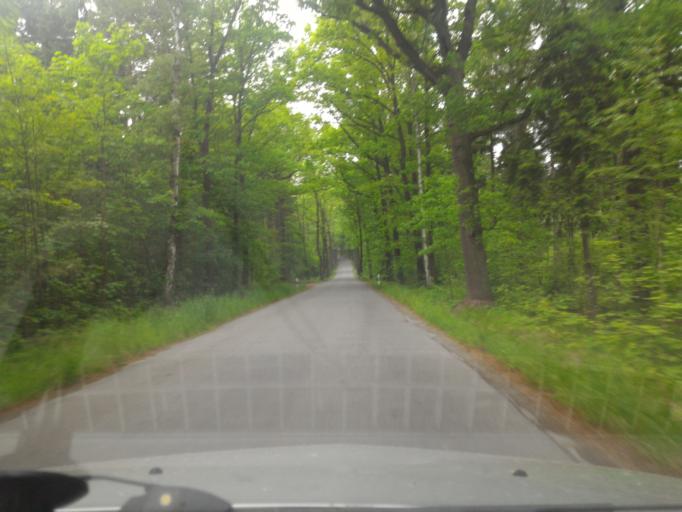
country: DE
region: Saxony
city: Olbersdorf
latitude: 50.8669
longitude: 14.7511
